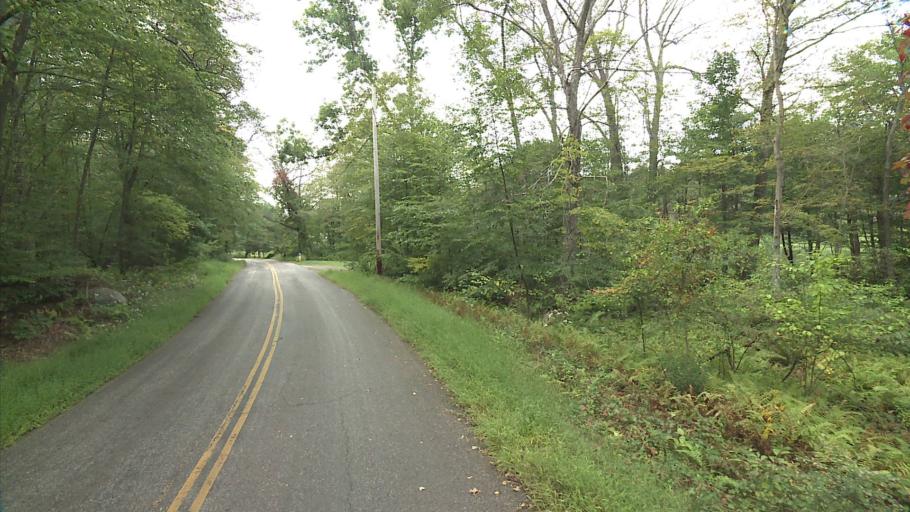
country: US
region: Connecticut
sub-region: Middlesex County
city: Higganum
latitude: 41.5245
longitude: -72.5324
